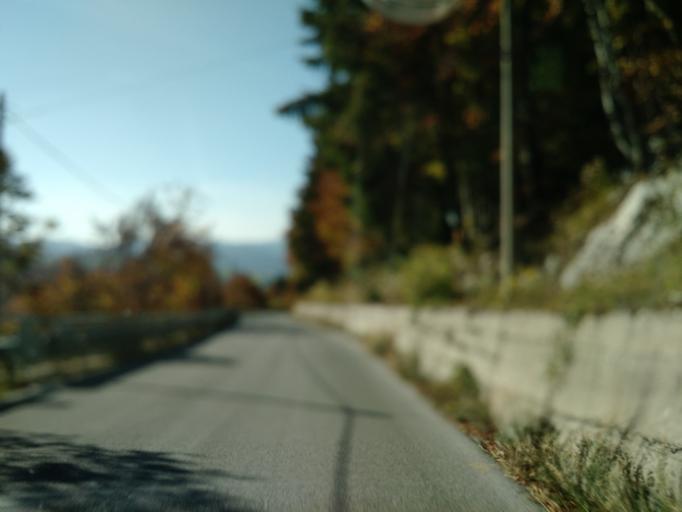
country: IT
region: Veneto
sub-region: Provincia di Vicenza
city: Gallio
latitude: 45.9027
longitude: 11.5652
